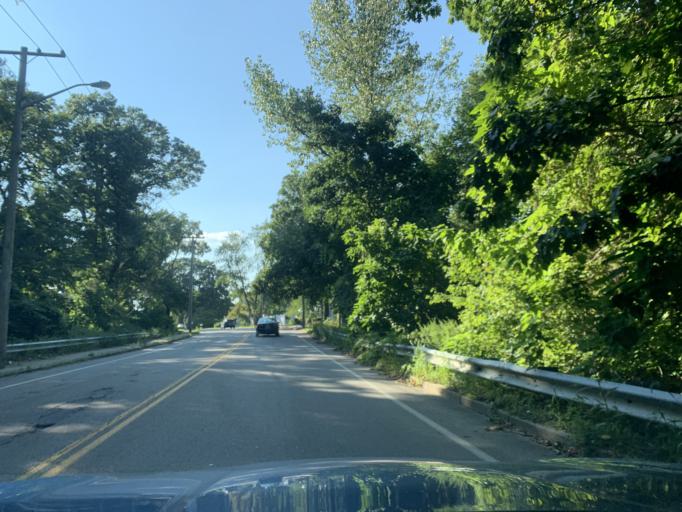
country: US
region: Rhode Island
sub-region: Kent County
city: West Warwick
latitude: 41.7089
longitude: -71.4869
